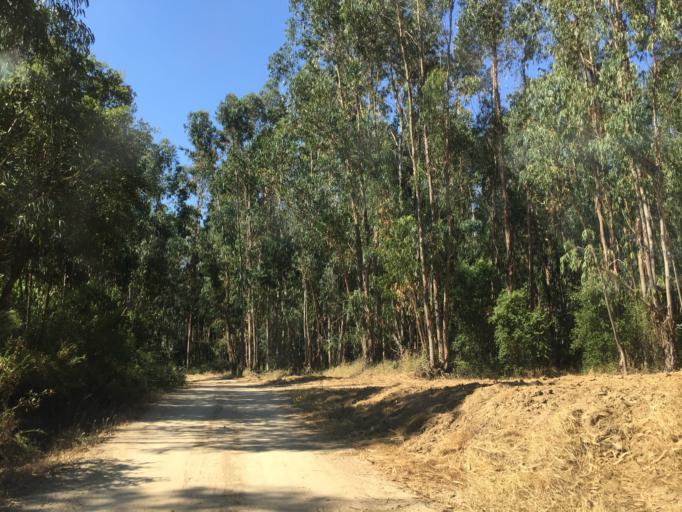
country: PT
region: Santarem
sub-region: Tomar
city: Tomar
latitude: 39.6126
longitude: -8.3536
